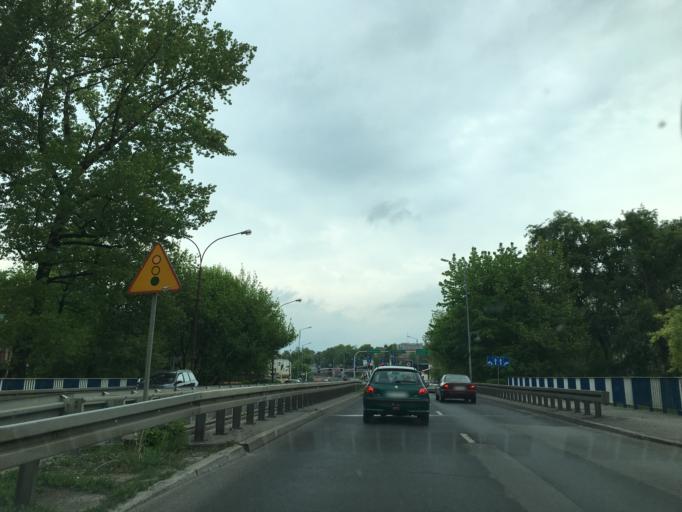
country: PL
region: Silesian Voivodeship
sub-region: Powiat bedzinski
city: Czeladz
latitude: 50.3177
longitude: 19.0681
